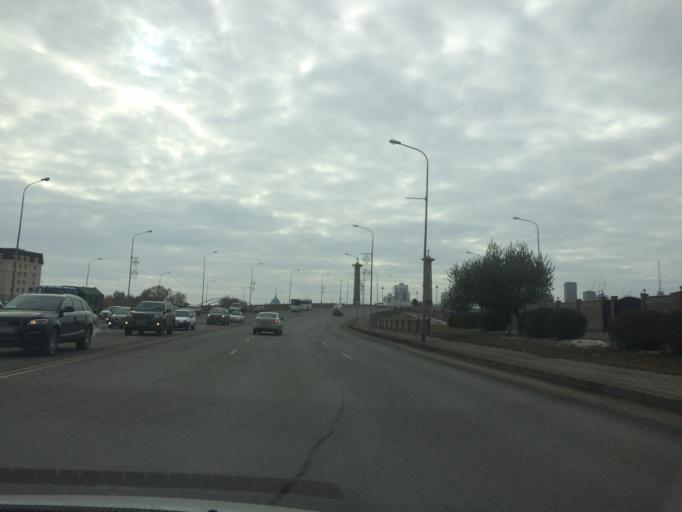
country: KZ
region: Astana Qalasy
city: Astana
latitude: 51.1416
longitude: 71.4451
